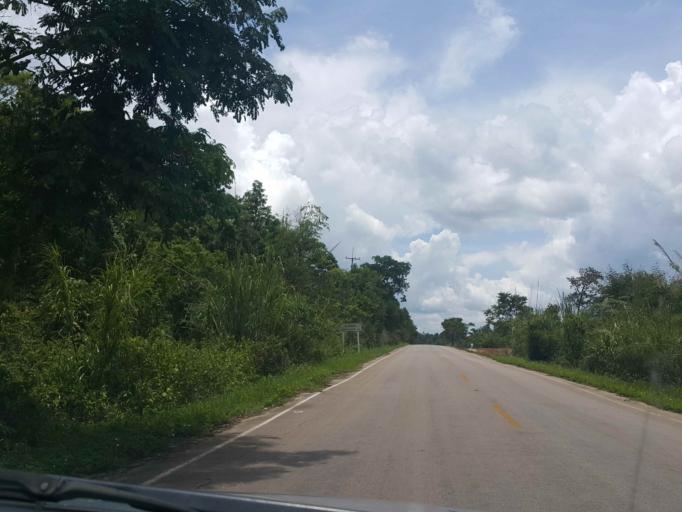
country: TH
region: Phayao
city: Chiang Muan
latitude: 18.8962
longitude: 100.1458
